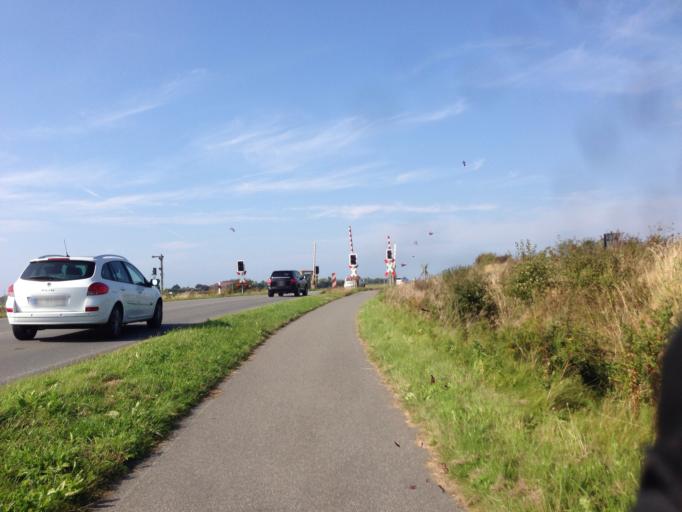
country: DE
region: Schleswig-Holstein
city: Keitum
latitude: 54.8918
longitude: 8.3602
